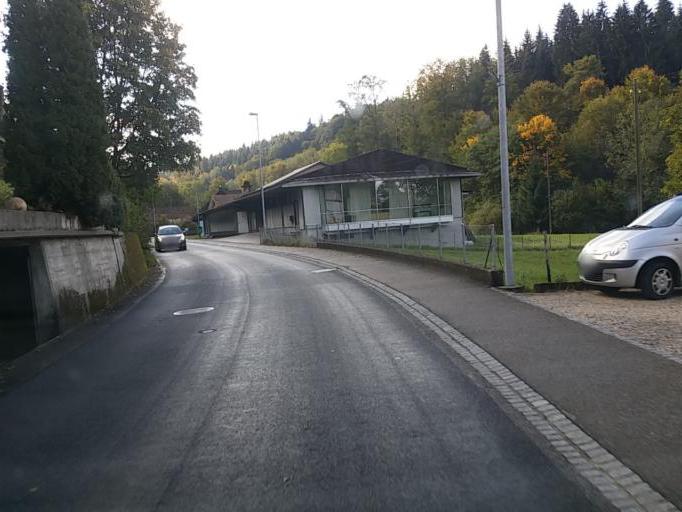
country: CH
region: Bern
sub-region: Oberaargau
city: Herzogenbuchsee
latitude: 47.1667
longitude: 7.7317
